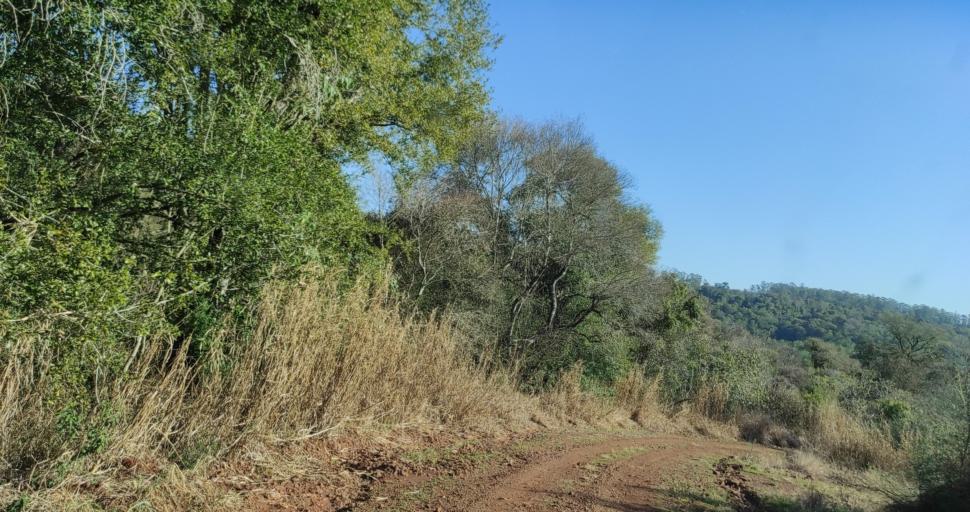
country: AR
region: Misiones
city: Capiovi
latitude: -26.9031
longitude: -55.1062
